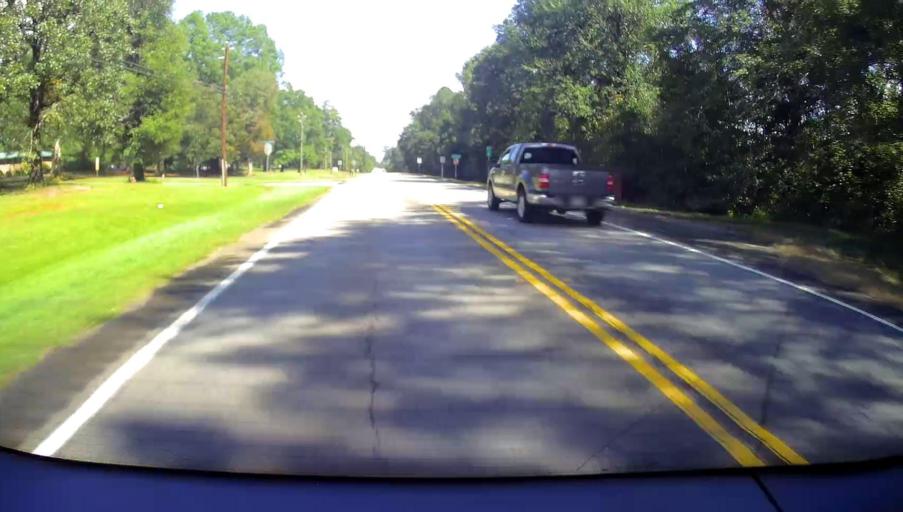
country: US
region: Georgia
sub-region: Jones County
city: Gray
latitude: 33.0311
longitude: -83.4363
